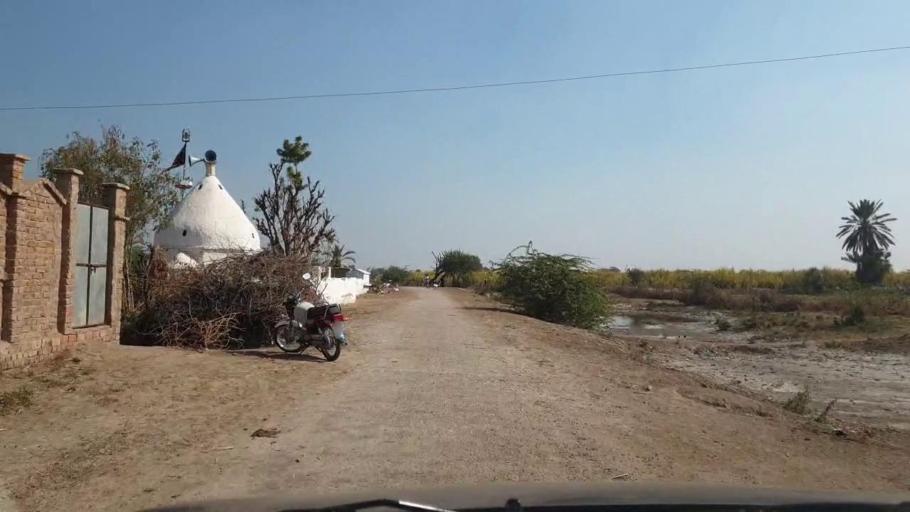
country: PK
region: Sindh
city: Jhol
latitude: 25.9087
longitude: 68.8080
